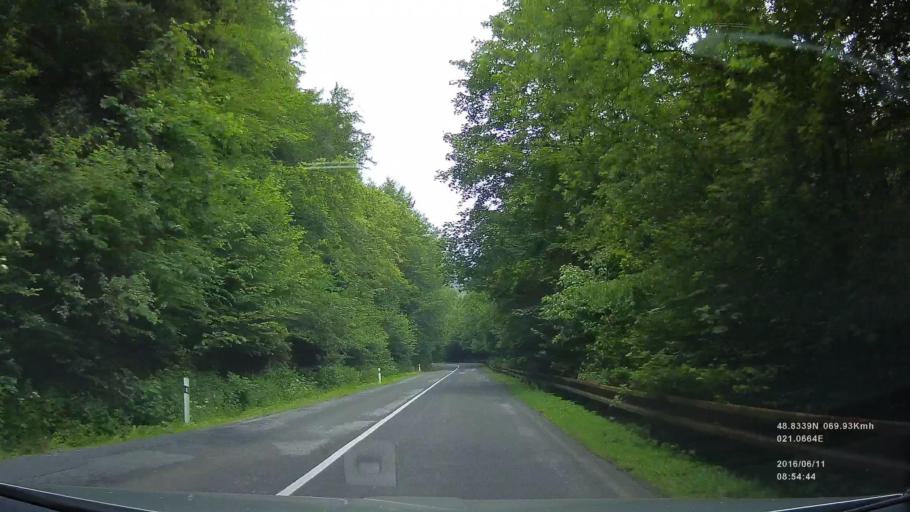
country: SK
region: Kosicky
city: Gelnica
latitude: 48.8337
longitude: 21.0723
